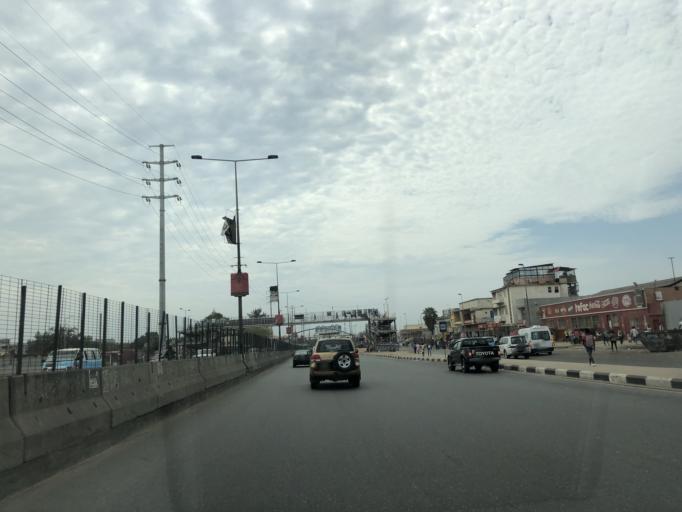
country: AO
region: Luanda
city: Luanda
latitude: -8.8379
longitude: 13.2625
